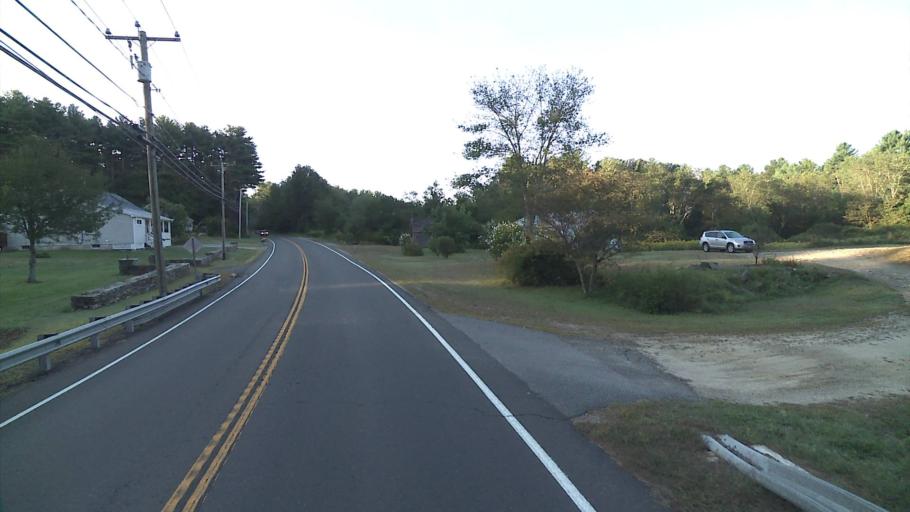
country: US
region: Connecticut
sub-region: Tolland County
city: Stafford
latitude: 41.9878
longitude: -72.3179
